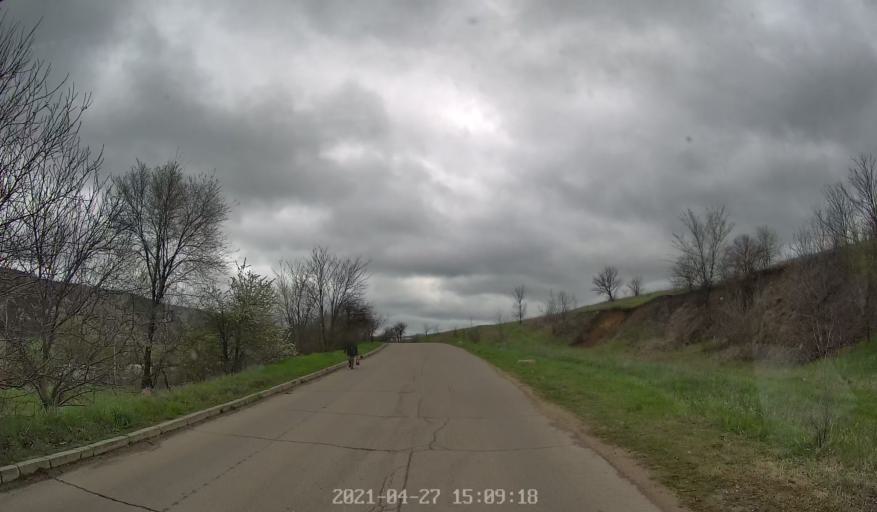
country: MD
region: Chisinau
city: Vadul lui Voda
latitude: 47.0509
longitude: 29.0342
